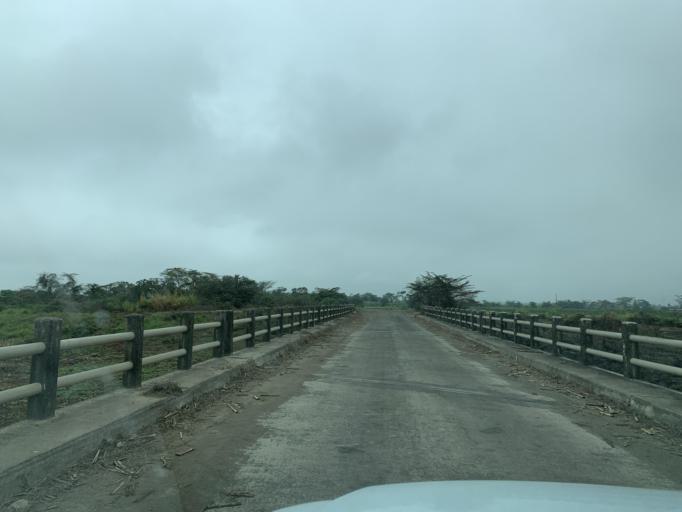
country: EC
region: Guayas
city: Coronel Marcelino Mariduena
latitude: -2.3586
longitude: -79.5831
